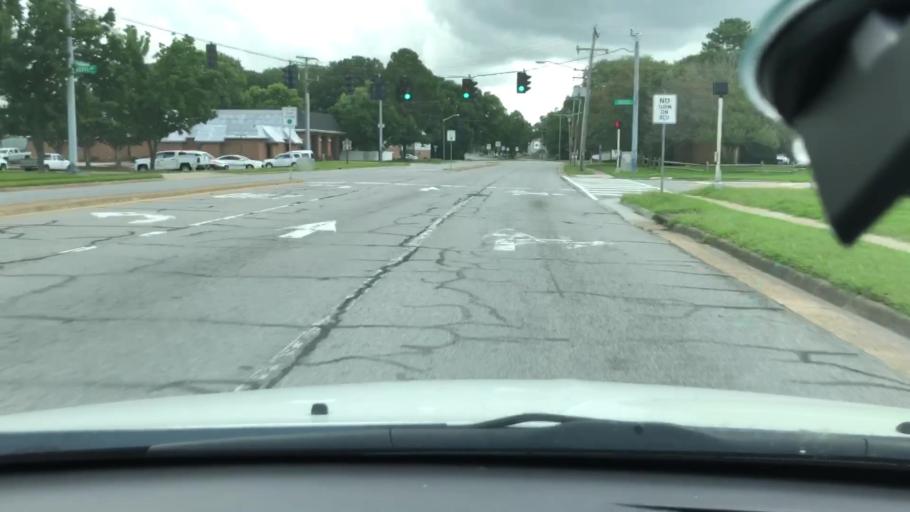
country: US
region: Virginia
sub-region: City of Chesapeake
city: Chesapeake
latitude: 36.8139
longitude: -76.1897
